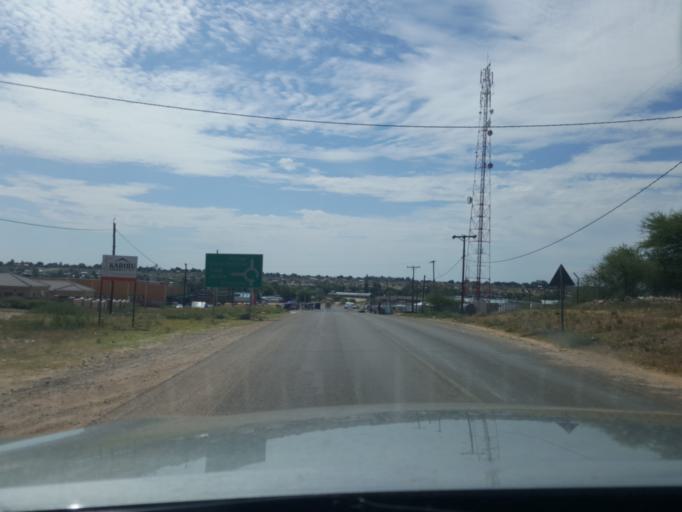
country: BW
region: Kweneng
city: Letlhakeng
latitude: -24.1033
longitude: 25.0311
